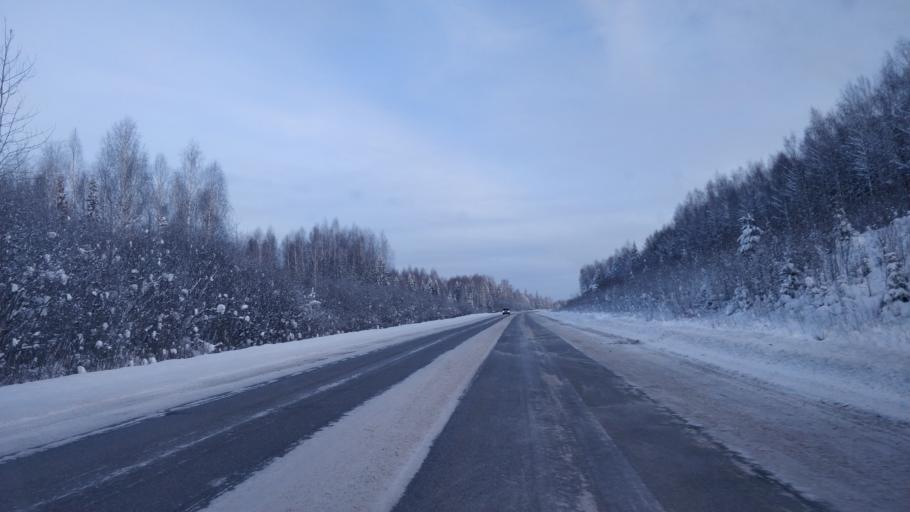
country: RU
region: Perm
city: Polazna
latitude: 58.2994
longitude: 56.5331
